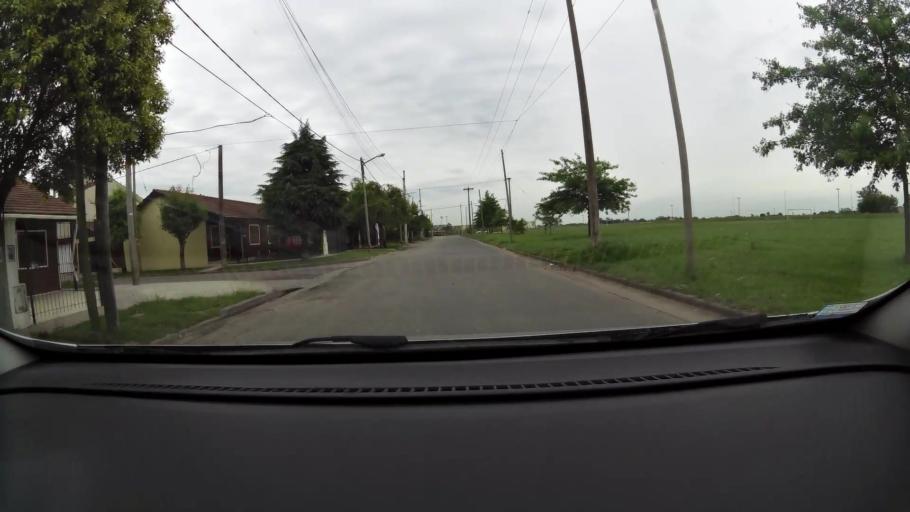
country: AR
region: Buenos Aires
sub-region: Partido de Campana
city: Campana
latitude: -34.1926
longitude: -58.9461
